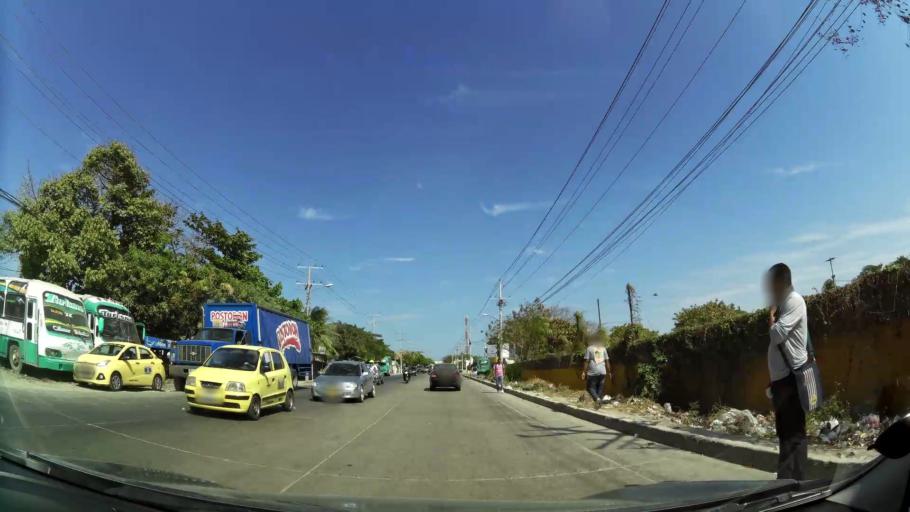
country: CO
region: Atlantico
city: Barranquilla
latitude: 10.9437
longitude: -74.8292
